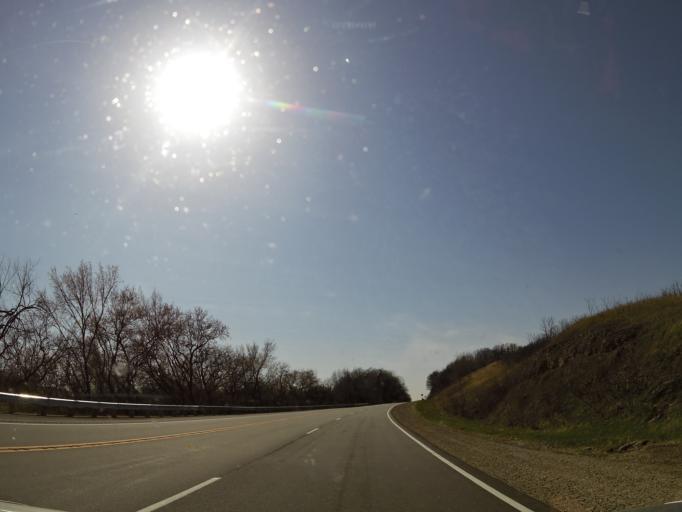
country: US
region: Wisconsin
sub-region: Pierce County
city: Ellsworth
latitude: 44.6835
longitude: -92.3718
